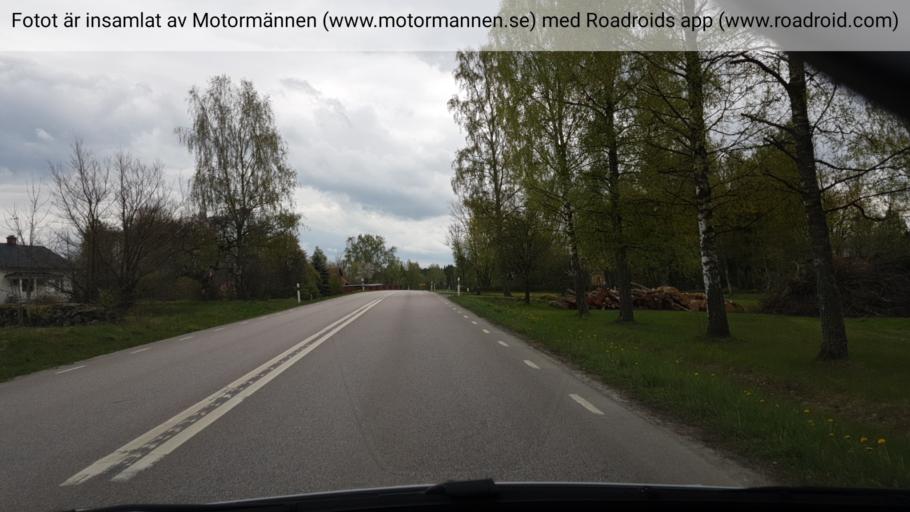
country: SE
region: Vaestra Goetaland
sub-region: Skara Kommun
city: Skara
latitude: 58.3300
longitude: 13.4360
